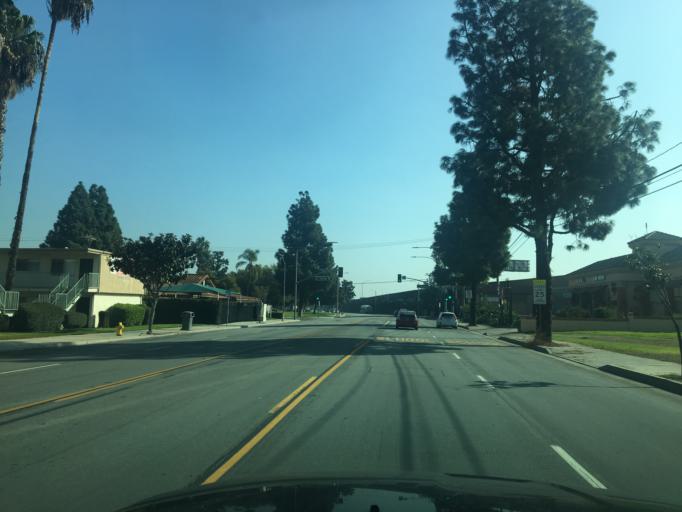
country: US
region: California
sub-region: Orange County
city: Tustin
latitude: 33.7375
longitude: -117.8213
